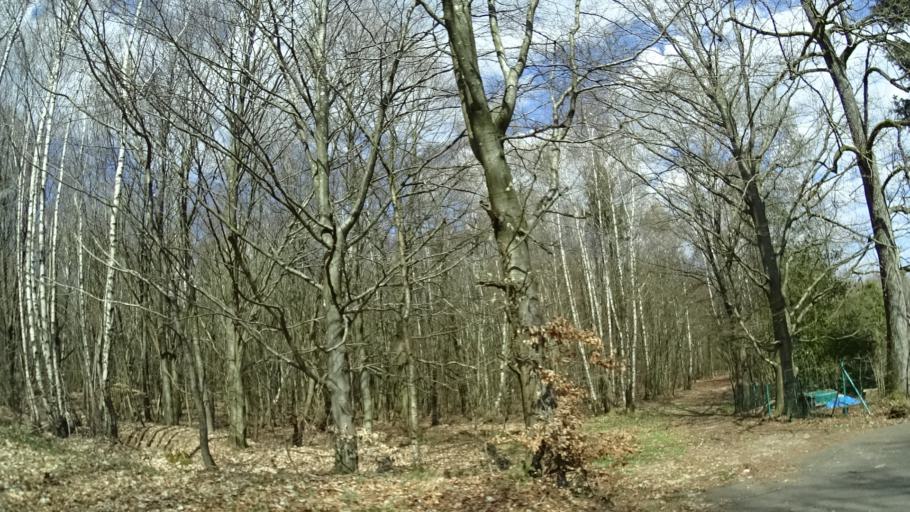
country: DE
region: Rheinland-Pfalz
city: Kirschweiler
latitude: 49.7533
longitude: 7.2361
